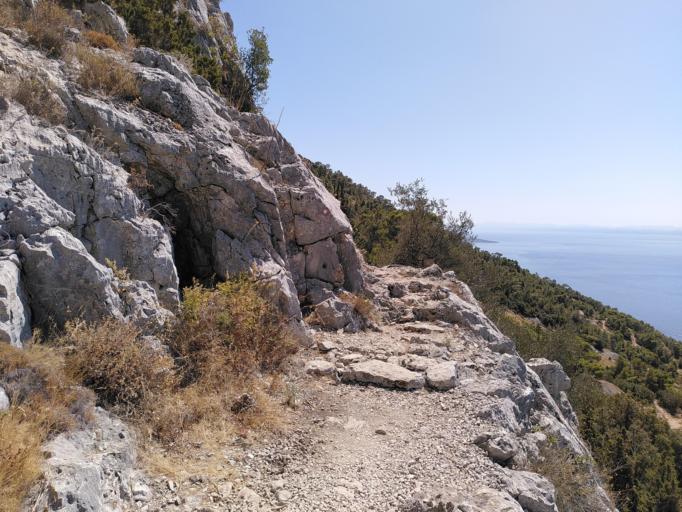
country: HR
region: Splitsko-Dalmatinska
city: Stari Grad
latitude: 43.1434
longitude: 16.5888
